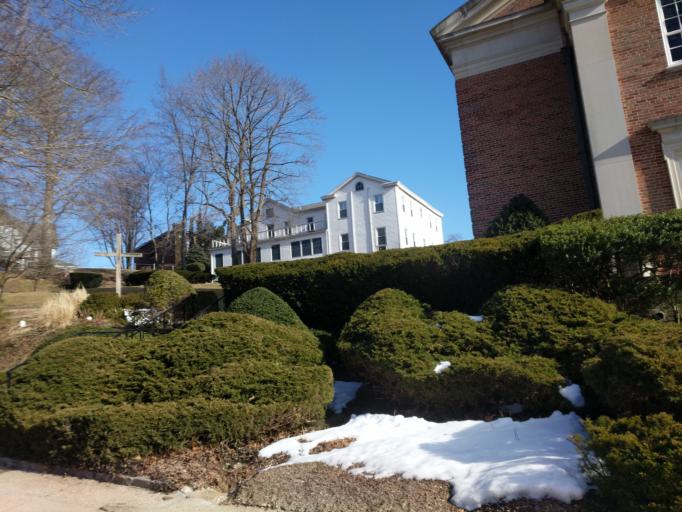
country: US
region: New York
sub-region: Suffolk County
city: Northport
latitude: 40.9014
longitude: -73.3428
